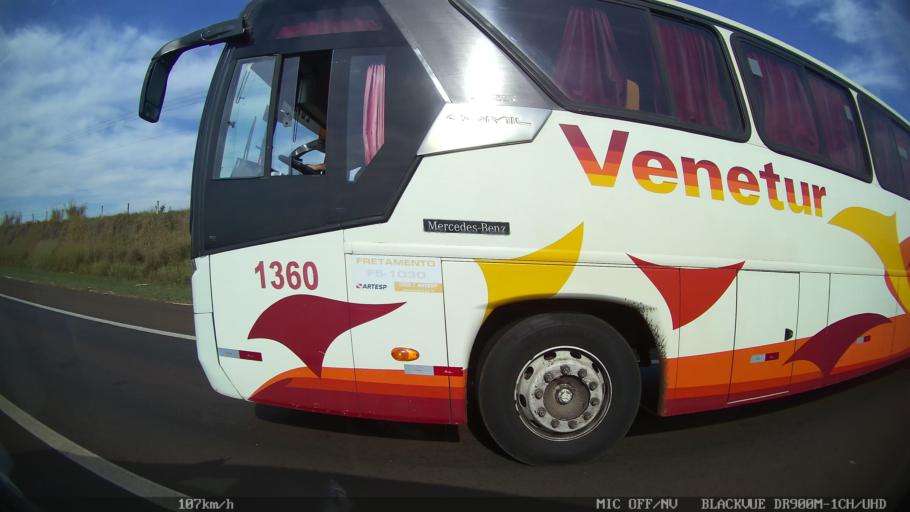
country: BR
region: Sao Paulo
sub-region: Araraquara
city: Araraquara
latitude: -21.7844
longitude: -48.1170
